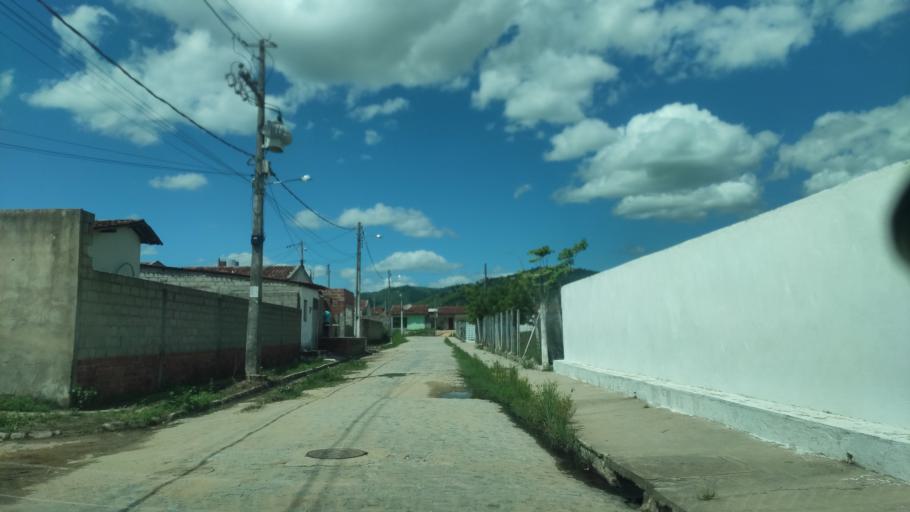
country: BR
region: Alagoas
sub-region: Uniao Dos Palmares
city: Uniao dos Palmares
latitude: -9.1454
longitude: -36.0017
